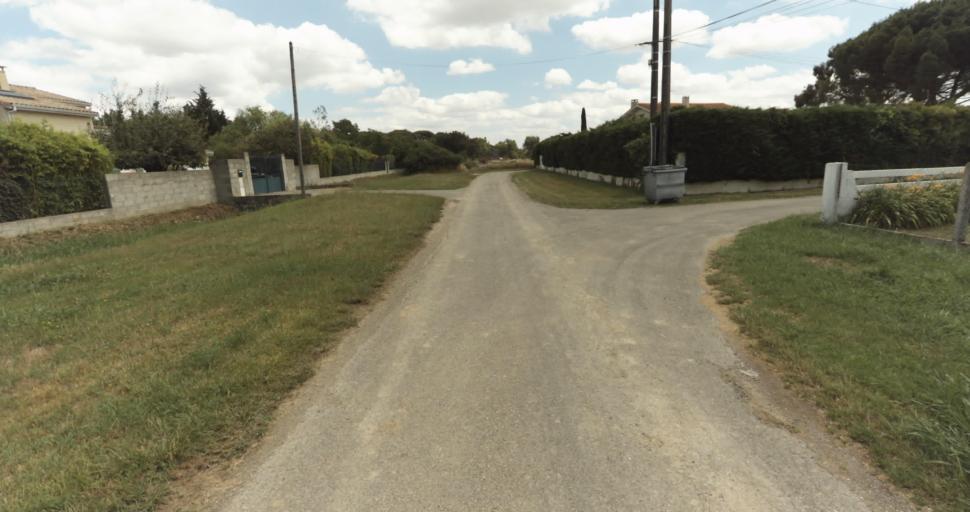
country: FR
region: Midi-Pyrenees
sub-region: Departement de la Haute-Garonne
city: Fontenilles
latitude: 43.5414
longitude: 1.1833
